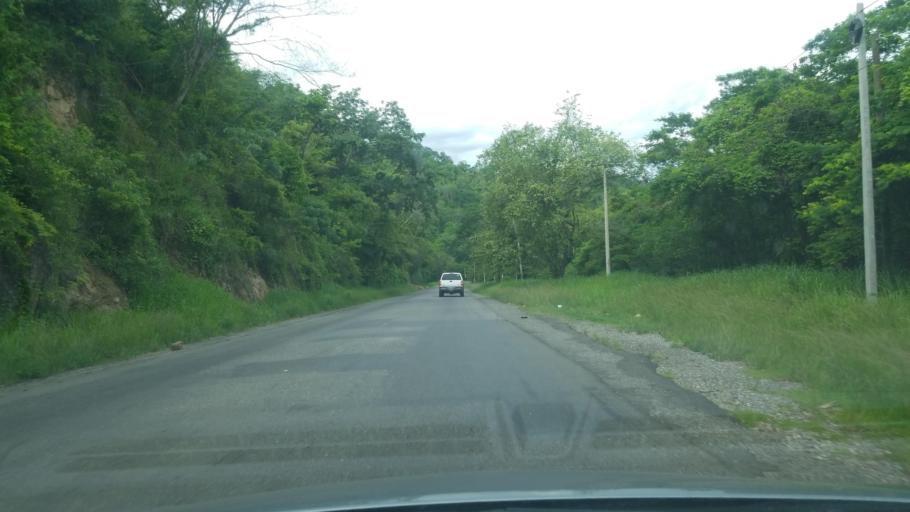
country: HN
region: Santa Barbara
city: Camalote
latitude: 15.3286
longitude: -88.3038
